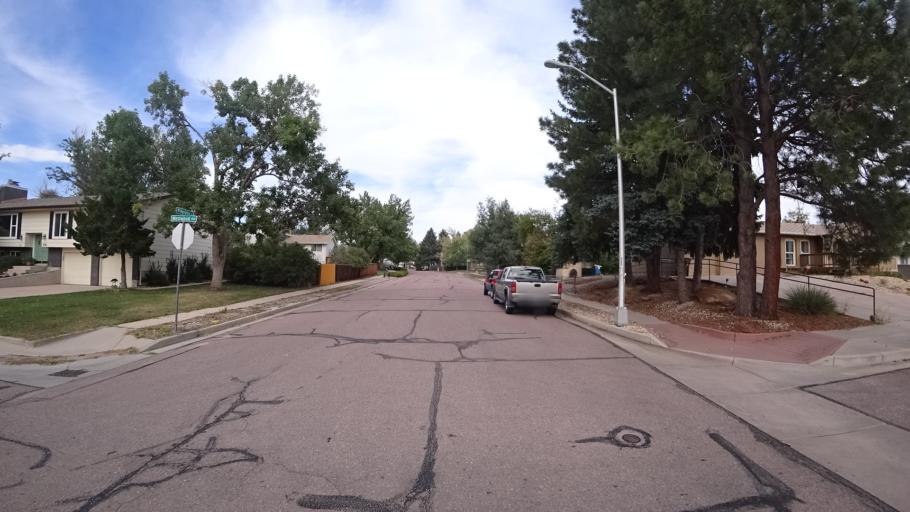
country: US
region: Colorado
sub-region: El Paso County
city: Colorado Springs
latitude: 38.8991
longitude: -104.7748
